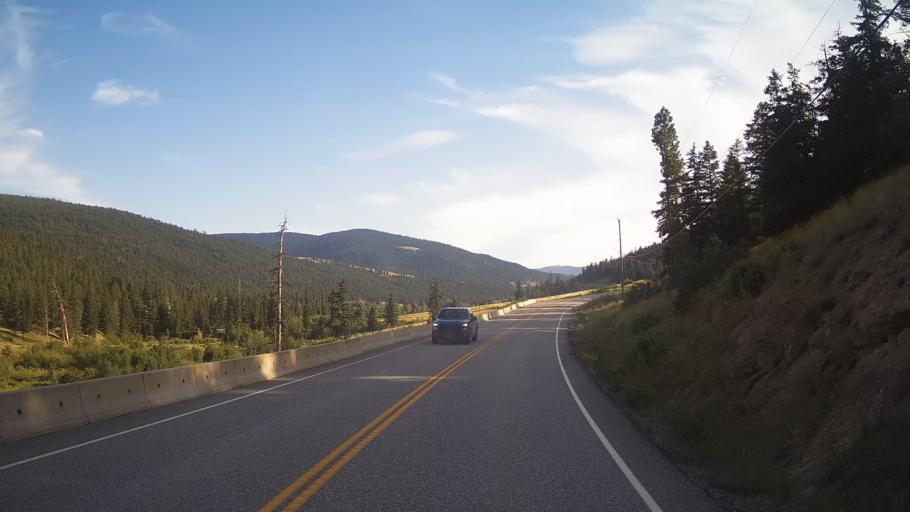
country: CA
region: British Columbia
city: Cache Creek
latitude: 50.8567
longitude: -121.5318
